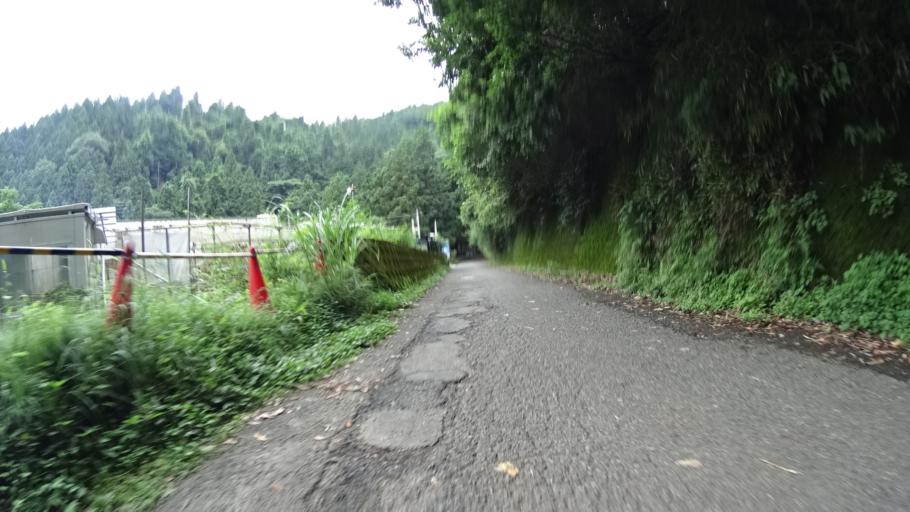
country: JP
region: Kanagawa
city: Atsugi
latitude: 35.5009
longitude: 139.2657
